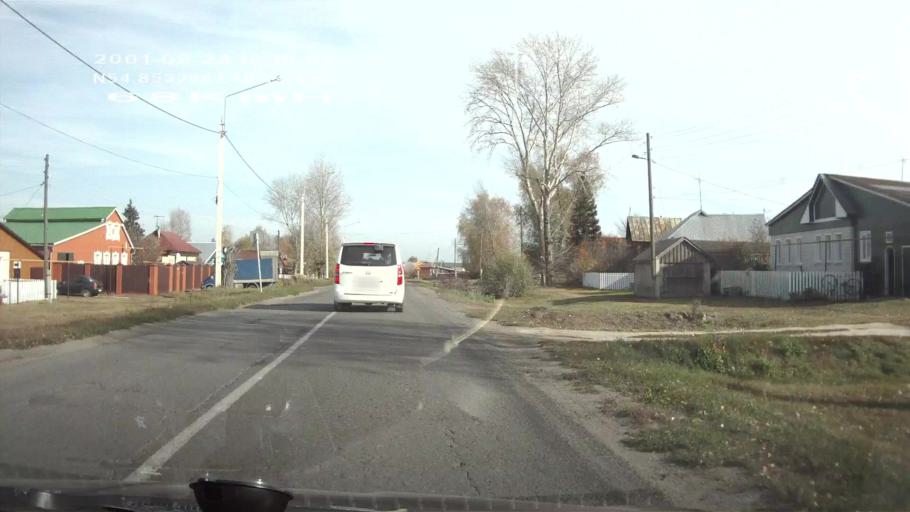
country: RU
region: Mordoviya
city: Turgenevo
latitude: 54.8533
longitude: 46.3979
